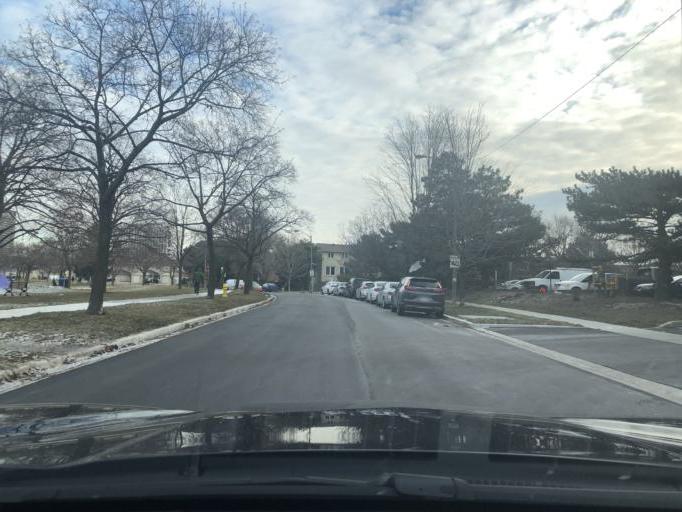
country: CA
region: Ontario
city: Willowdale
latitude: 43.7696
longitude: -79.3423
